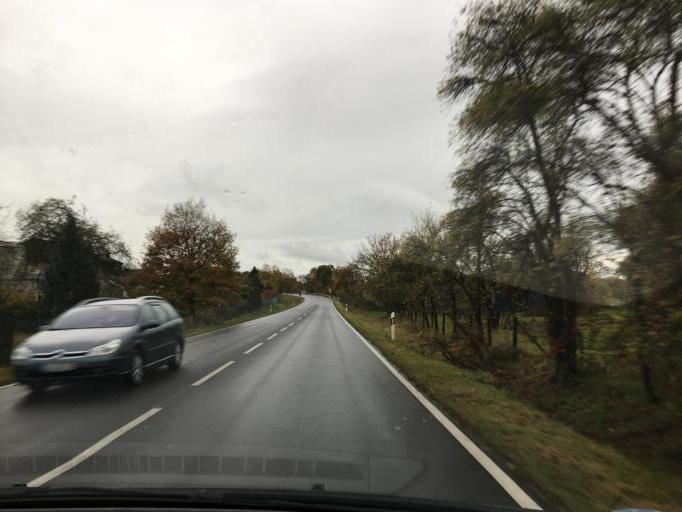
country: DE
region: North Rhine-Westphalia
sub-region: Regierungsbezirk Koln
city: Nideggen
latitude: 50.6539
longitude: 6.5465
